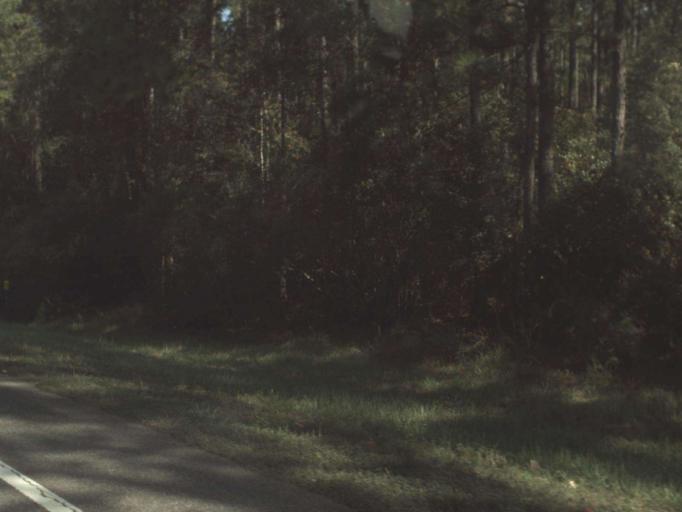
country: US
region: Florida
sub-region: Walton County
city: DeFuniak Springs
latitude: 30.8795
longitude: -86.1242
